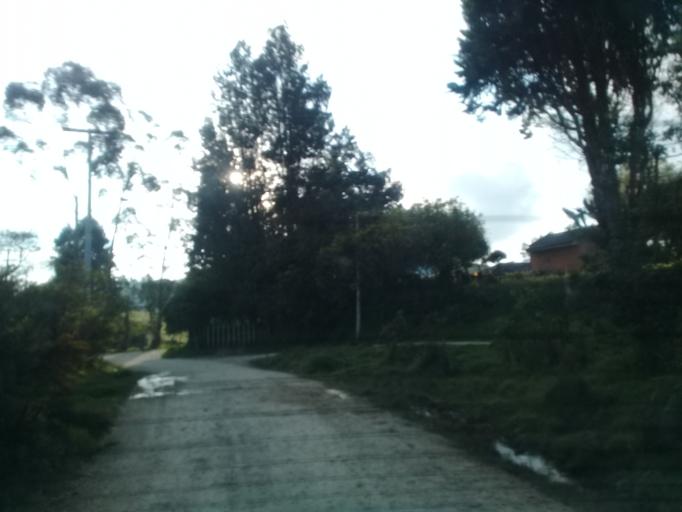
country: CO
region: Cundinamarca
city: Sibate
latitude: 4.4498
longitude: -74.2743
